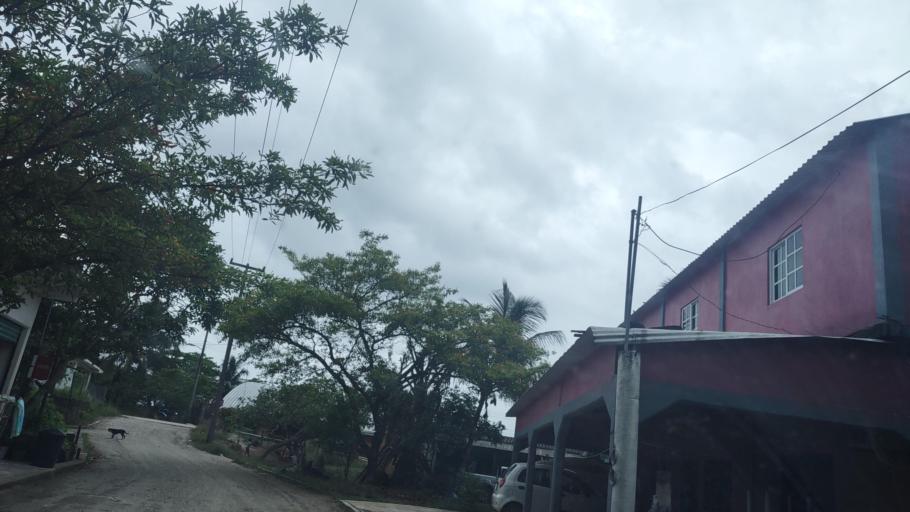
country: MX
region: Veracruz
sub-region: Uxpanapa
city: Poblado 10
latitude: 17.4971
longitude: -94.1621
